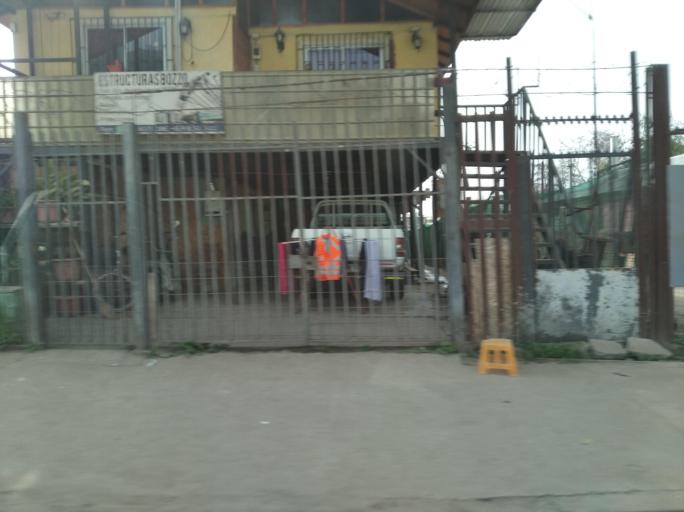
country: CL
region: Santiago Metropolitan
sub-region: Provincia de Chacabuco
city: Lampa
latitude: -33.2896
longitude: -70.8865
